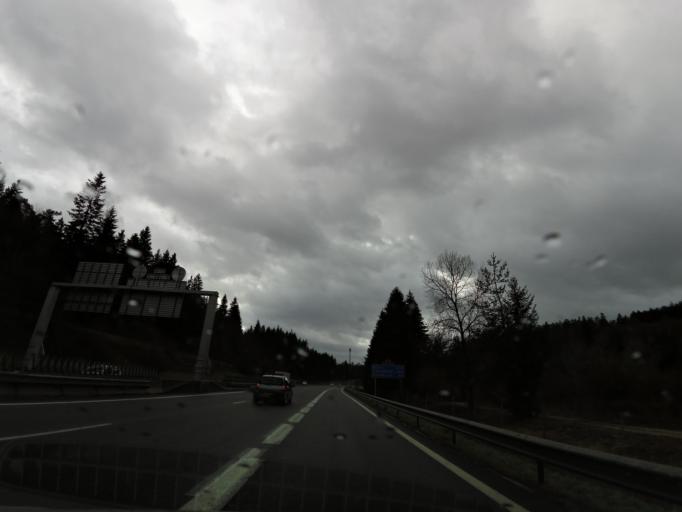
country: FR
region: Rhone-Alpes
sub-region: Departement de l'Ain
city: Saint-Martin-du-Frene
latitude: 46.1348
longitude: 5.5236
